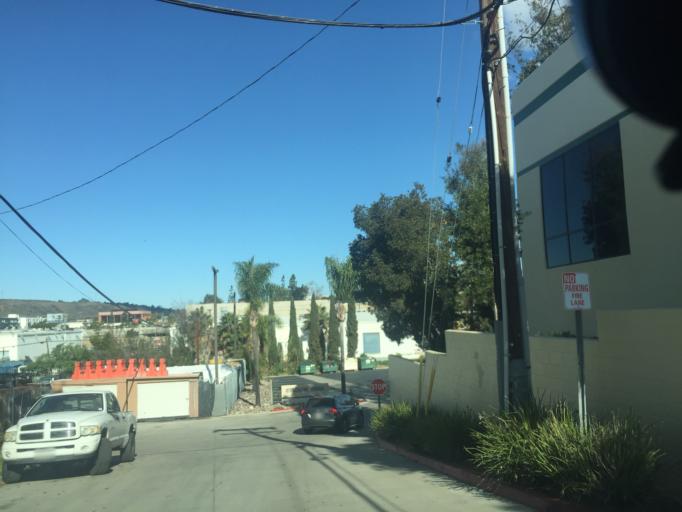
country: US
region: California
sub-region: San Diego County
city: La Mesa
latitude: 32.7814
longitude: -117.0969
